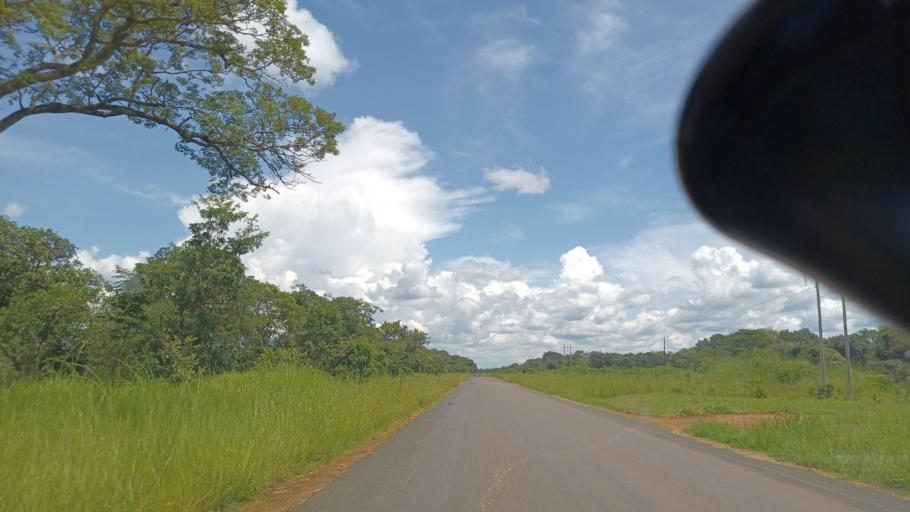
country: ZM
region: North-Western
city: Solwezi
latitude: -12.5663
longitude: 26.1383
